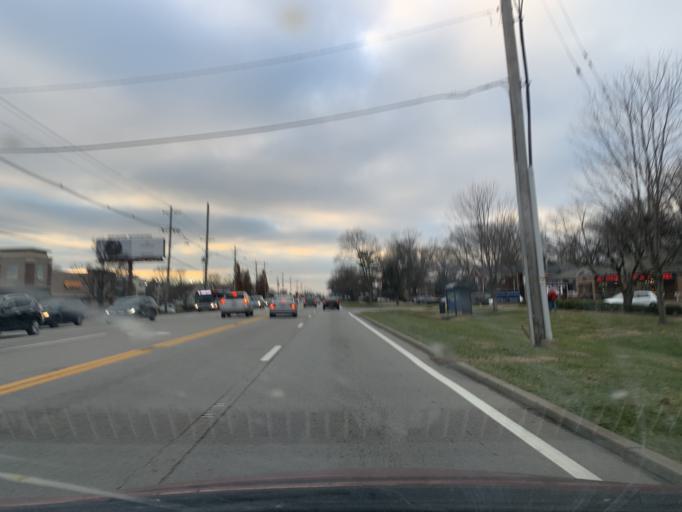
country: US
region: Kentucky
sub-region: Jefferson County
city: Beechwood Village
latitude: 38.2509
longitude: -85.6305
